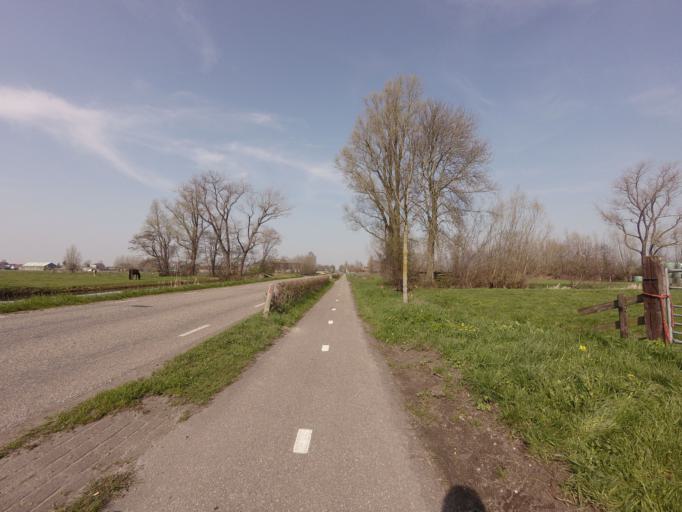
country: NL
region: Utrecht
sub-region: Stichtse Vecht
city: Breukelen
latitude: 52.1496
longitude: 4.9706
